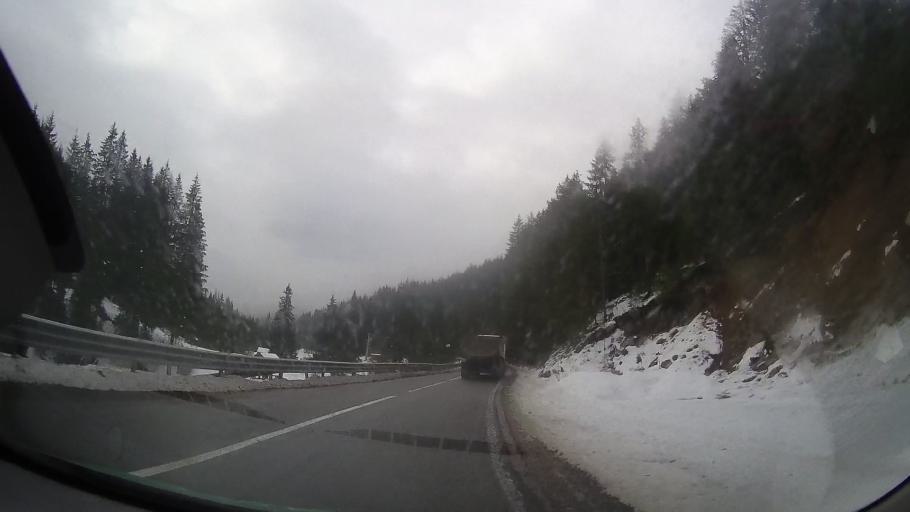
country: RO
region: Neamt
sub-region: Comuna Bicaz Chei
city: Bicaz Chei
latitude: 46.7801
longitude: 25.7574
